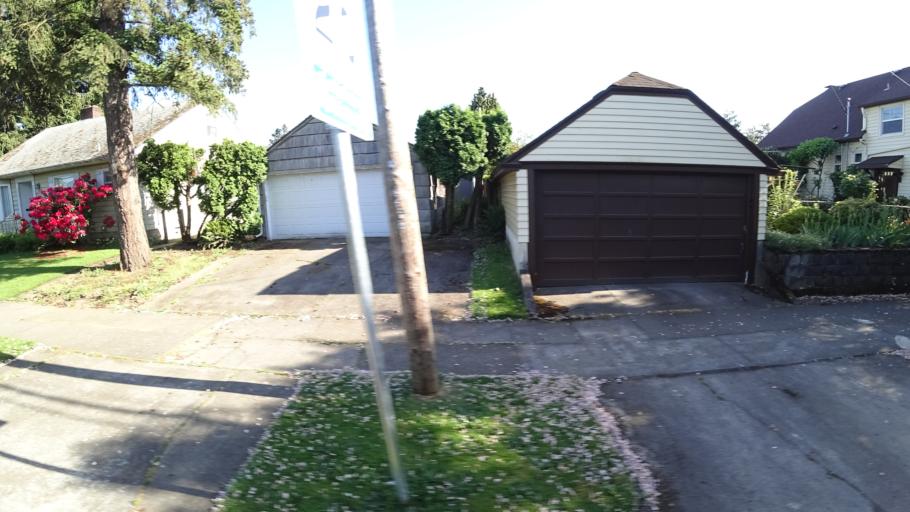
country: US
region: Oregon
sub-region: Multnomah County
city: Portland
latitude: 45.5546
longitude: -122.6847
